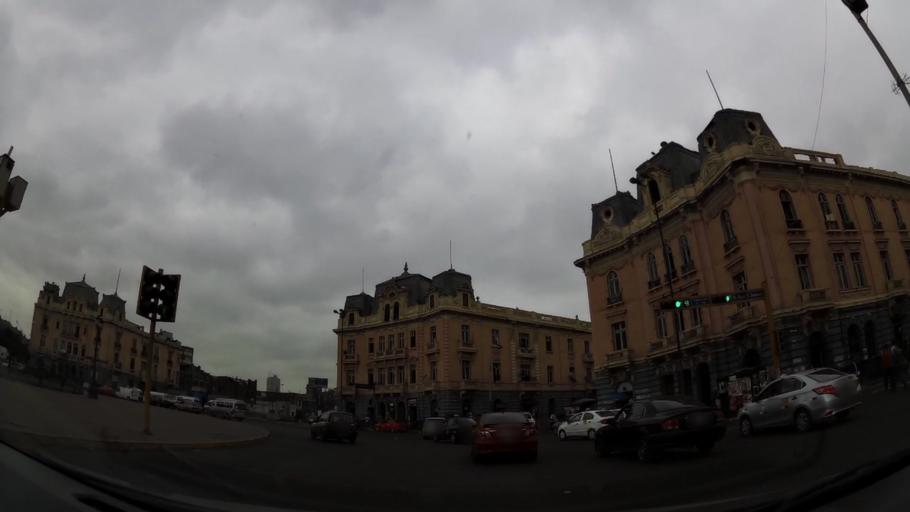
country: PE
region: Lima
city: Lima
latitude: -12.0464
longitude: -77.0432
